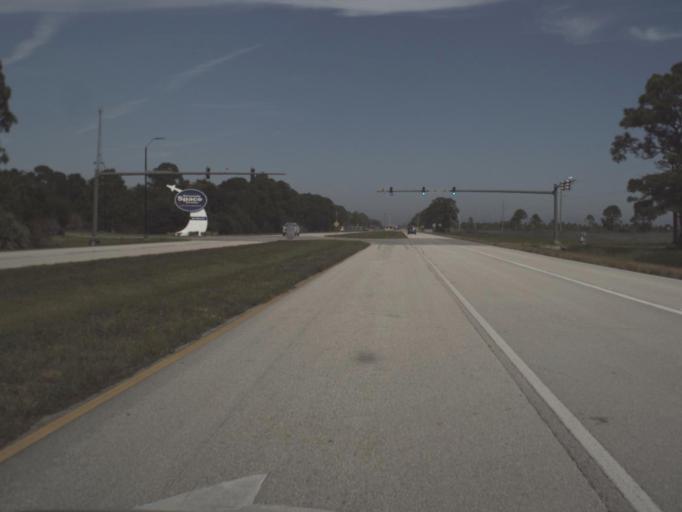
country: US
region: Florida
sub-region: Brevard County
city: Merritt Island
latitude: 28.4996
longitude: -80.6724
